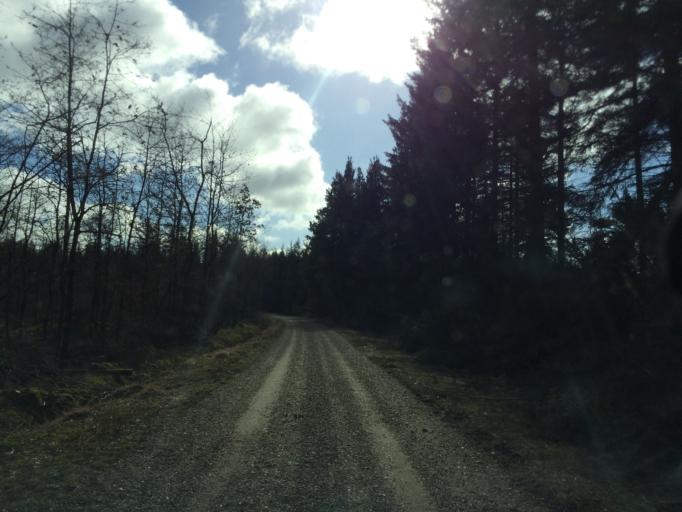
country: DK
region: Central Jutland
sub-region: Holstebro Kommune
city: Ulfborg
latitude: 56.2753
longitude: 8.4238
